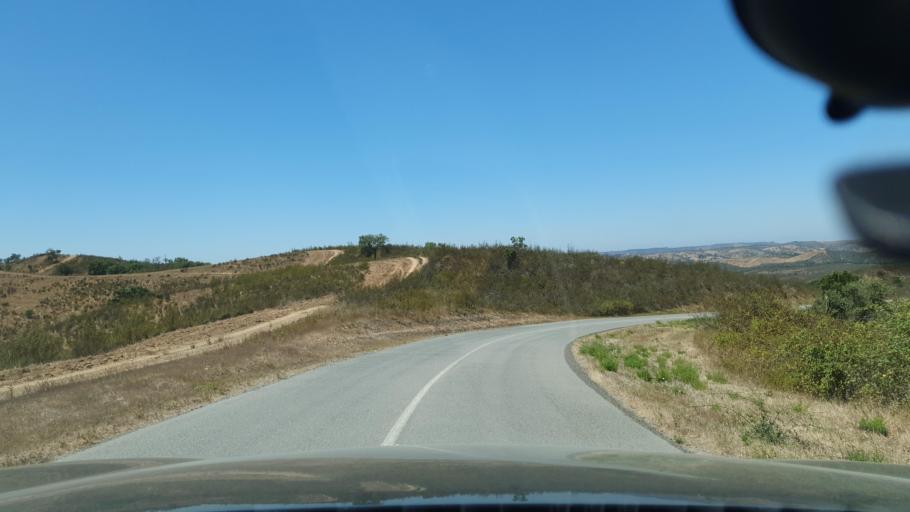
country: PT
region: Beja
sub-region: Odemira
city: Odemira
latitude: 37.5525
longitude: -8.4413
